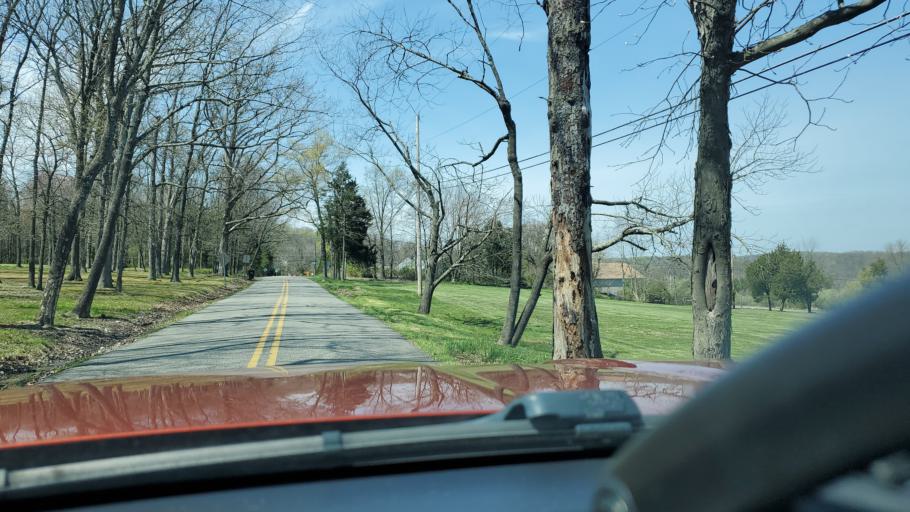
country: US
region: Pennsylvania
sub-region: Montgomery County
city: Gilbertsville
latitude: 40.3367
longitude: -75.5468
